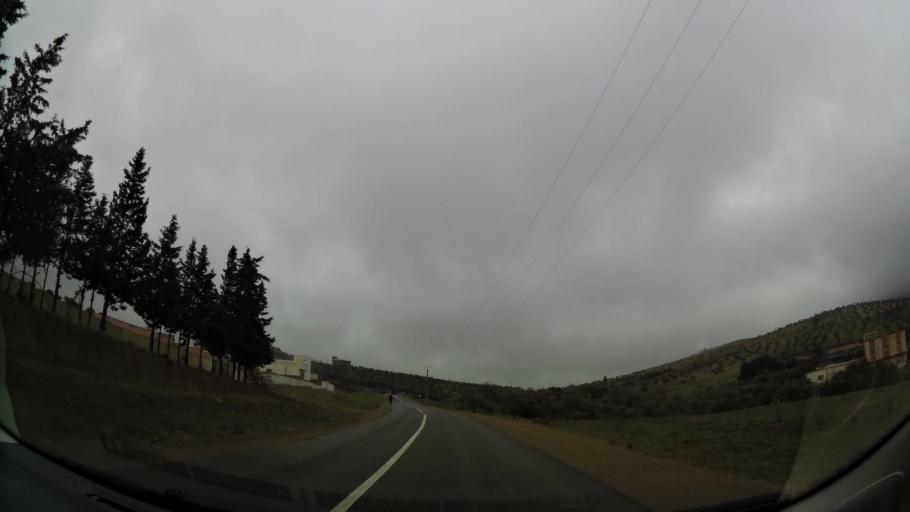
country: MA
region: Oriental
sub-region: Nador
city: Selouane
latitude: 35.1246
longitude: -3.0611
